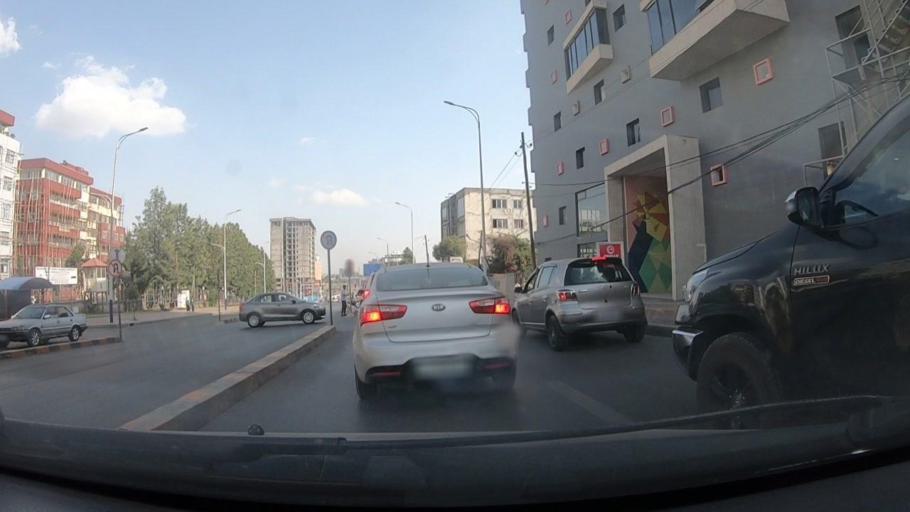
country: ET
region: Adis Abeba
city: Addis Ababa
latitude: 8.9910
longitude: 38.7404
